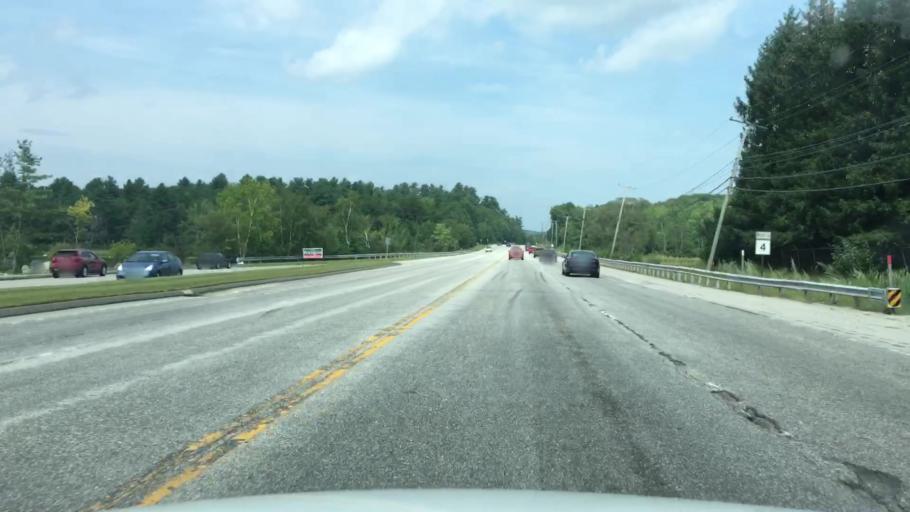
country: US
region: Maine
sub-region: Androscoggin County
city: Lewiston
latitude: 44.1449
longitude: -70.2278
